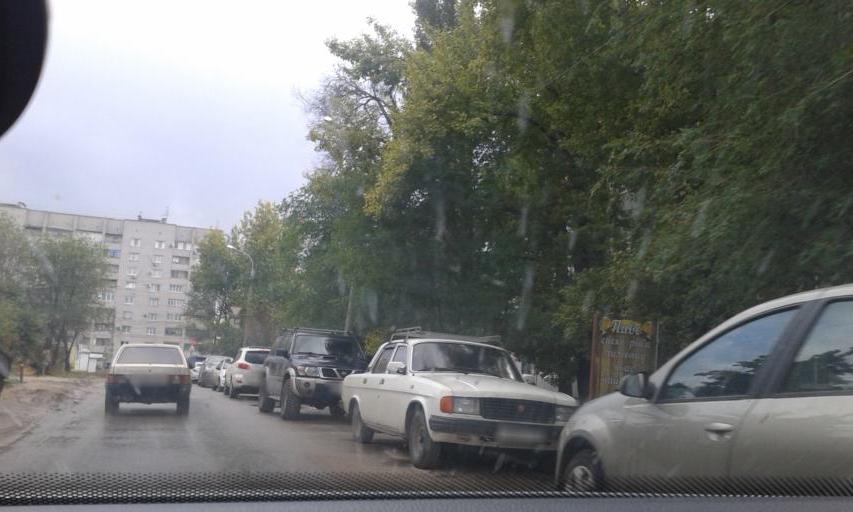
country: RU
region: Volgograd
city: Gorodishche
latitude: 48.7691
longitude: 44.4925
